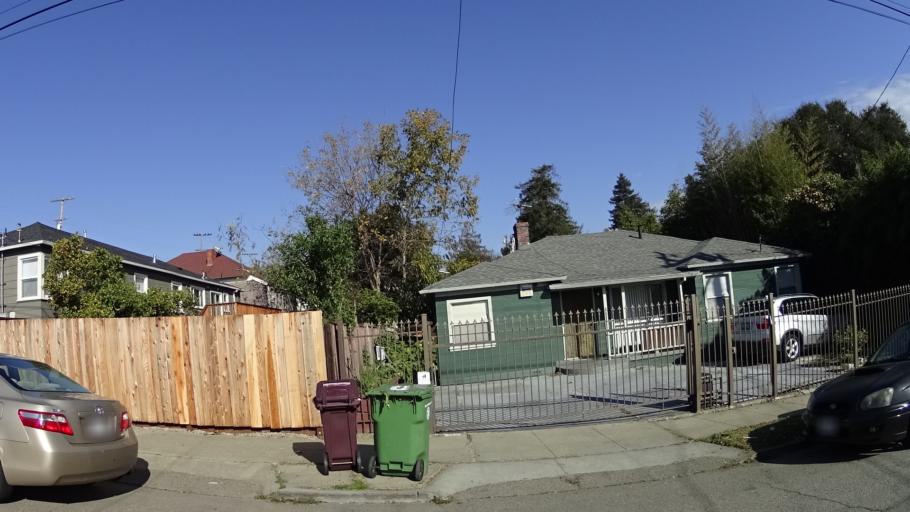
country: US
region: California
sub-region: Alameda County
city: Alameda
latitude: 37.7920
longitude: -122.2352
